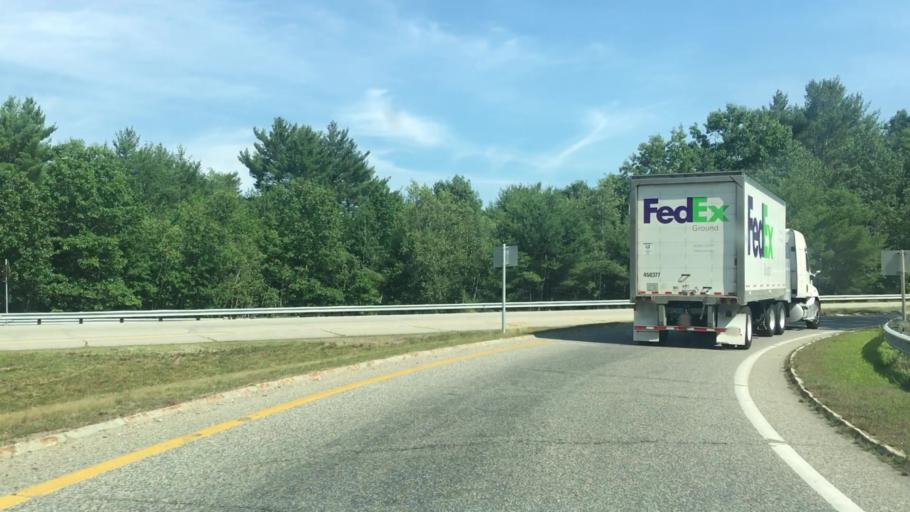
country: US
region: New Hampshire
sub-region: Strafford County
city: Rochester
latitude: 43.3325
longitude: -70.9731
